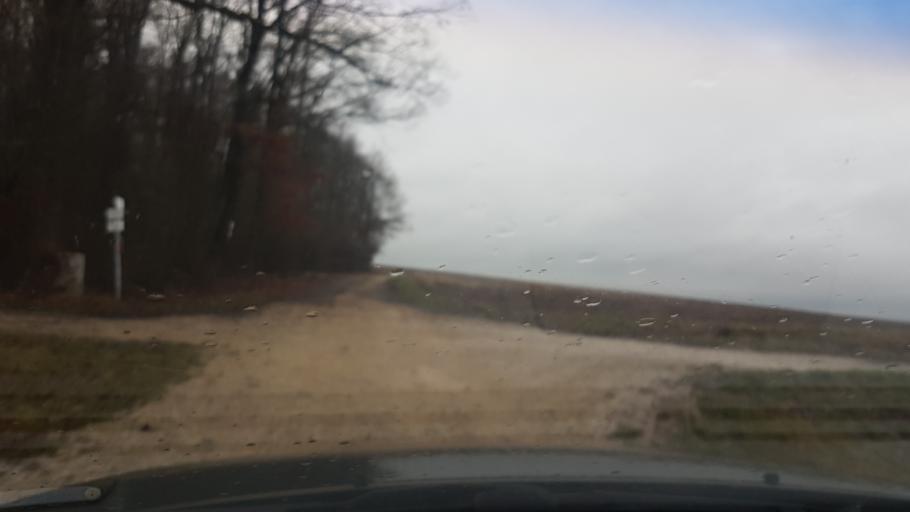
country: DE
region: Bavaria
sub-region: Upper Franconia
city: Zapfendorf
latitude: 50.0287
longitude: 10.9608
